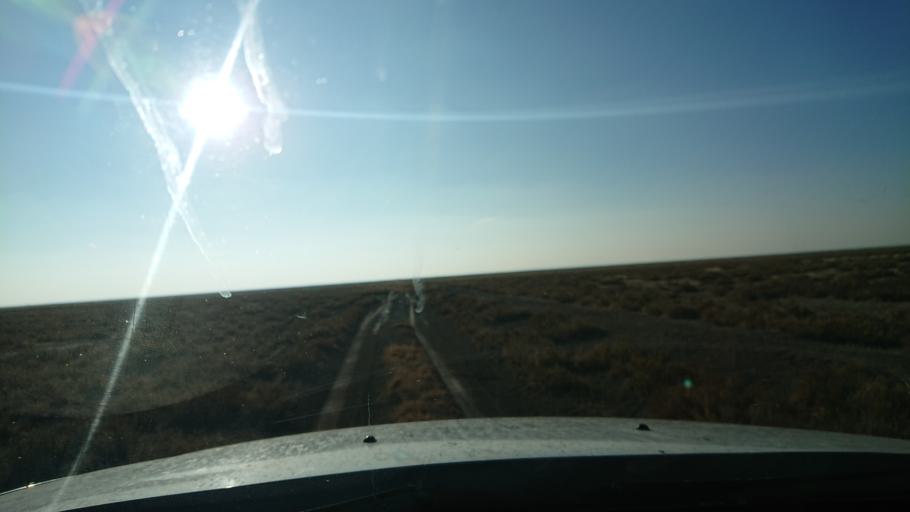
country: TR
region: Aksaray
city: Sultanhani
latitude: 38.3824
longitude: 33.5810
